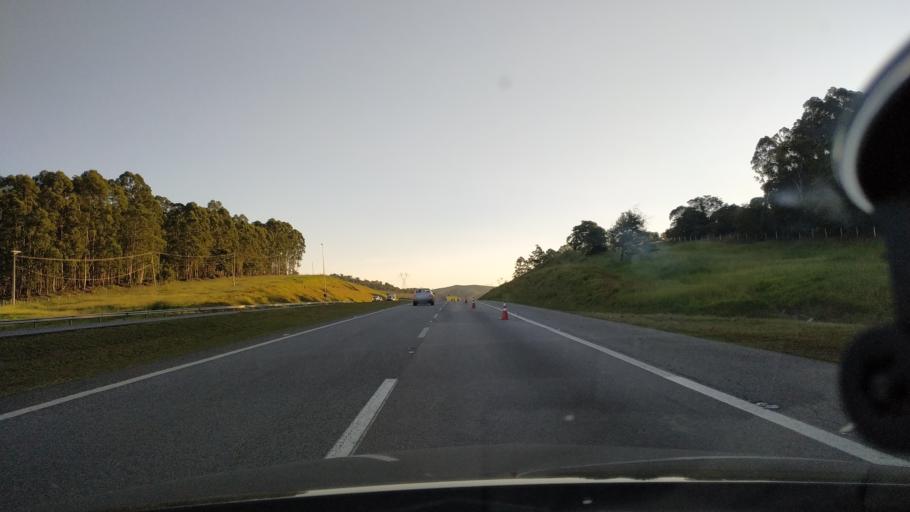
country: BR
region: Sao Paulo
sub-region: Sao Jose Dos Campos
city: Sao Jose dos Campos
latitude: -23.2442
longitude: -45.7901
